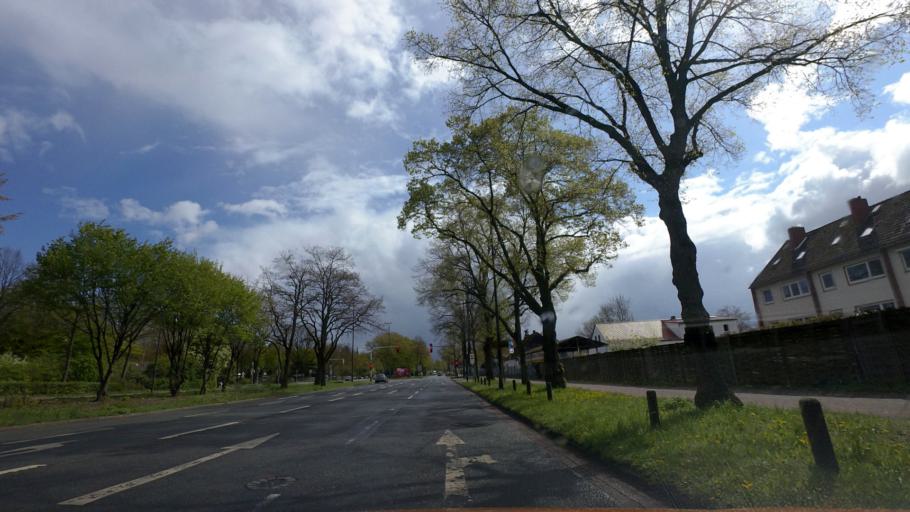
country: DE
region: Lower Saxony
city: Lilienthal
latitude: 53.0595
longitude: 8.9128
